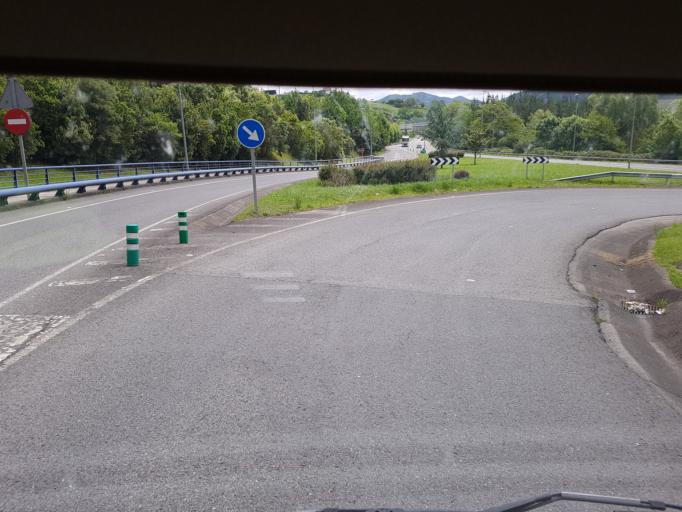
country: ES
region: Basque Country
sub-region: Bizkaia
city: Durango
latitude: 43.1735
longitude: -2.6175
